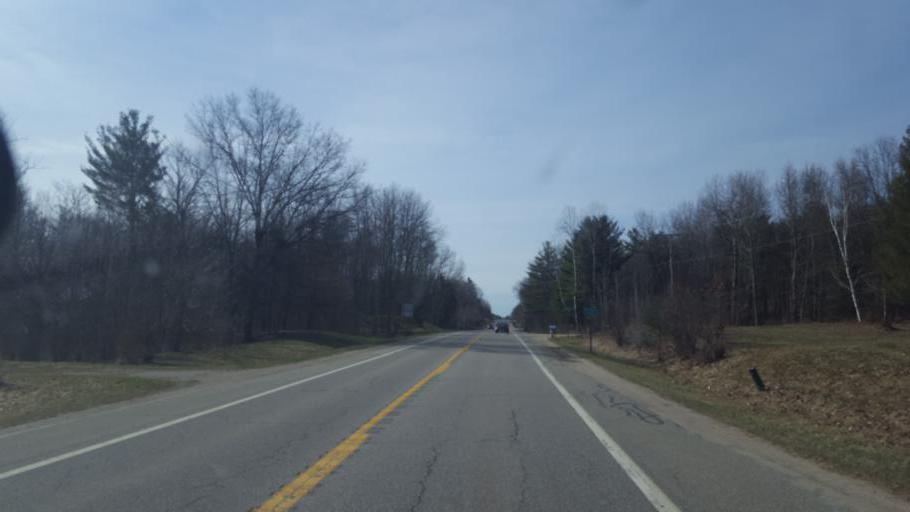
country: US
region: Michigan
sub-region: Mecosta County
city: Big Rapids
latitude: 43.5808
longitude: -85.5626
